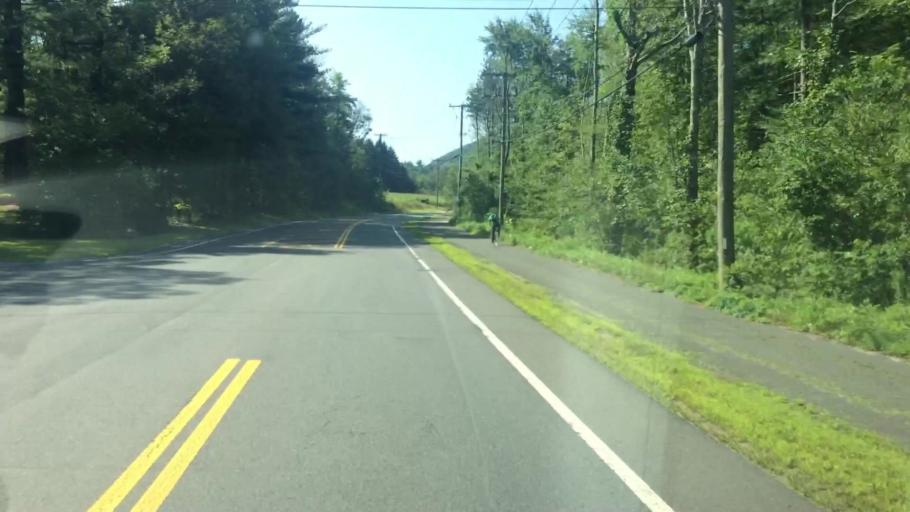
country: US
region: Massachusetts
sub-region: Hampshire County
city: South Amherst
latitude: 42.3228
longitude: -72.5249
